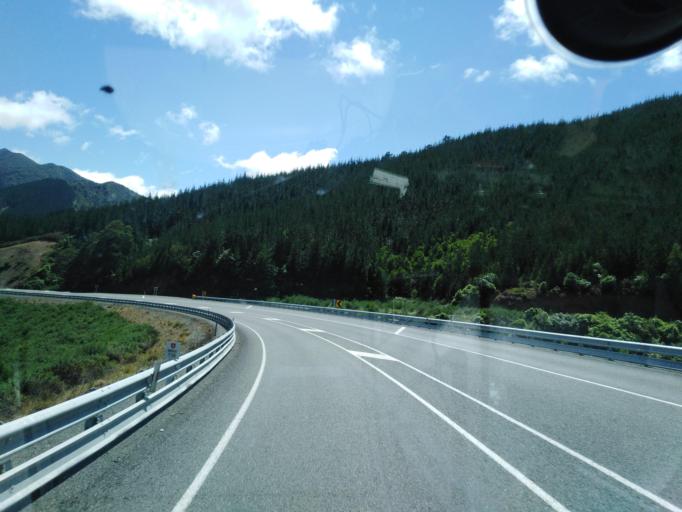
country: NZ
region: Nelson
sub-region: Nelson City
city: Nelson
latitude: -41.1853
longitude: 173.5592
